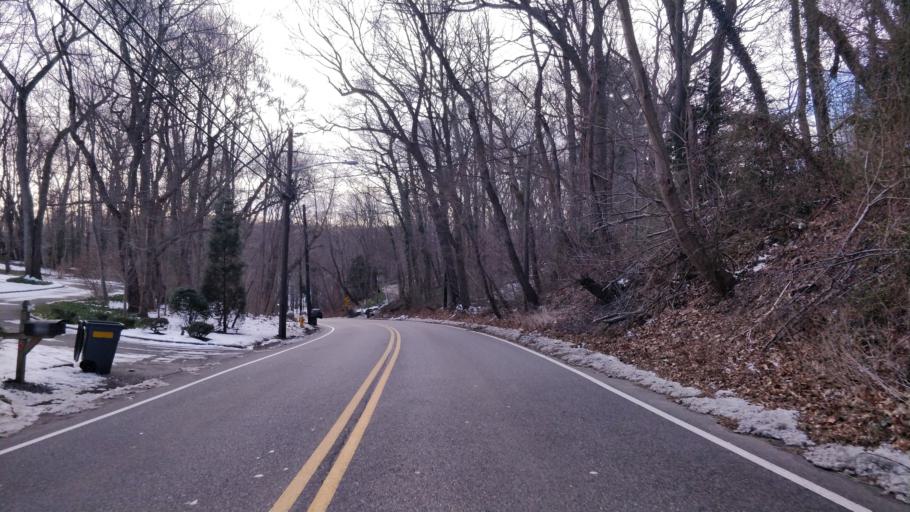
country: US
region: New York
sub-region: Suffolk County
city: Cold Spring Harbor
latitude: 40.8649
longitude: -73.4443
